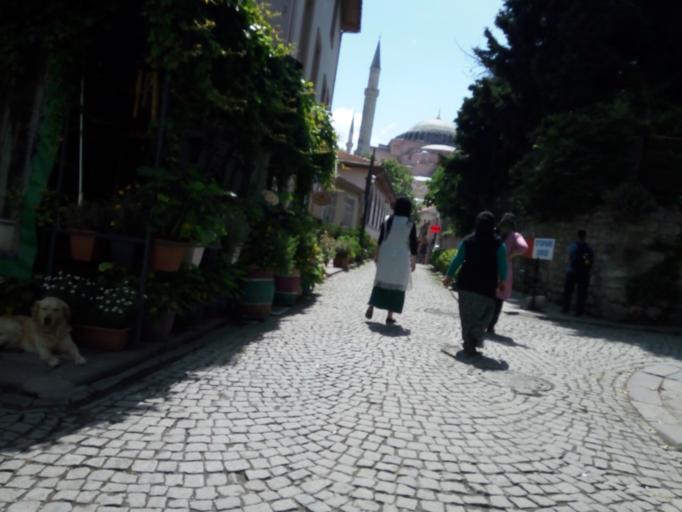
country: TR
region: Istanbul
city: Eminoenue
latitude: 41.0101
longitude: 28.9778
